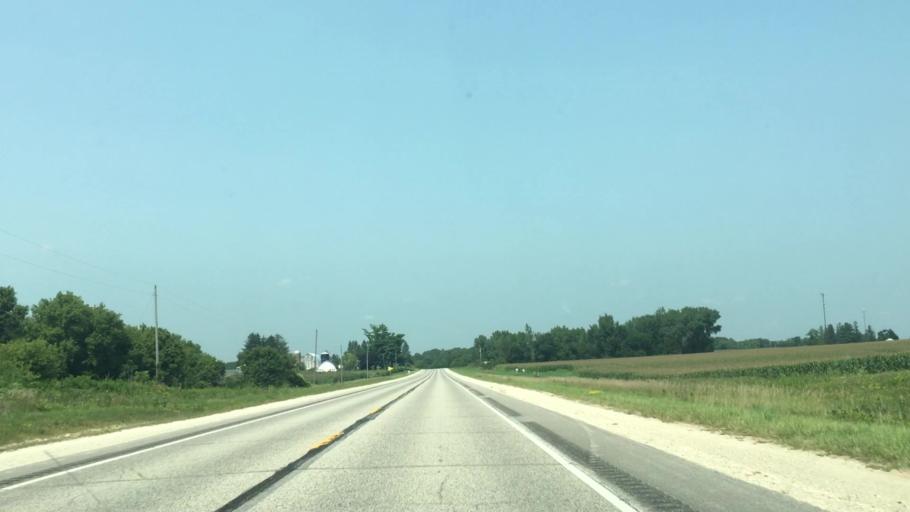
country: US
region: Iowa
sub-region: Fayette County
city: Fayette
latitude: 42.8220
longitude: -91.8050
